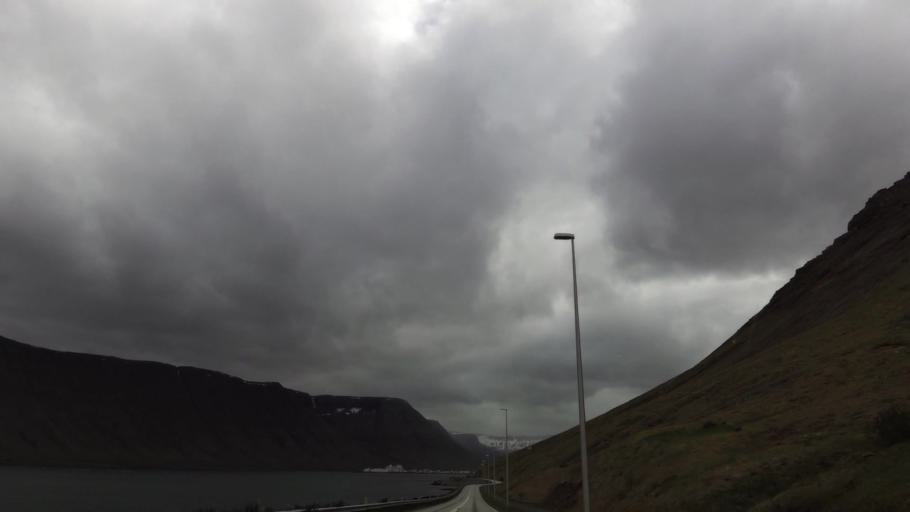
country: IS
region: Westfjords
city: Isafjoerdur
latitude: 66.0985
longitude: -23.1102
